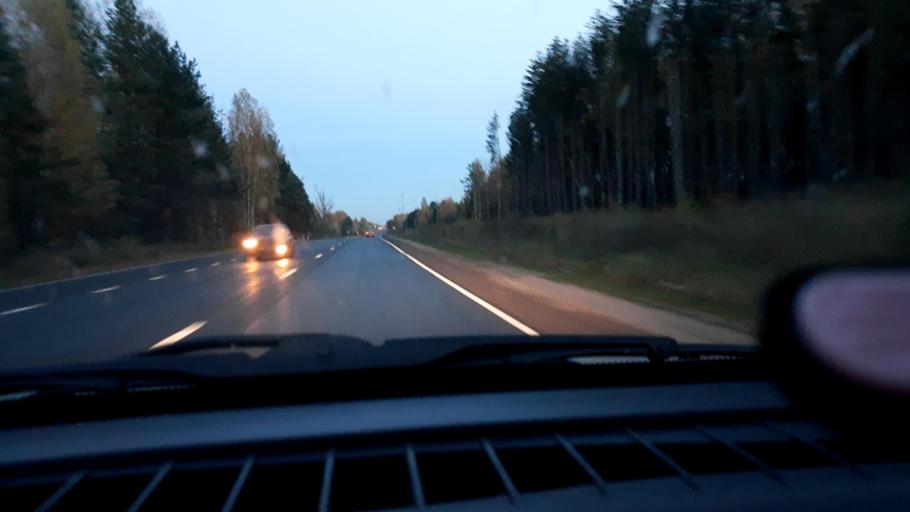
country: RU
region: Nizjnij Novgorod
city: Novaya Balakhna
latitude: 56.6069
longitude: 43.6148
